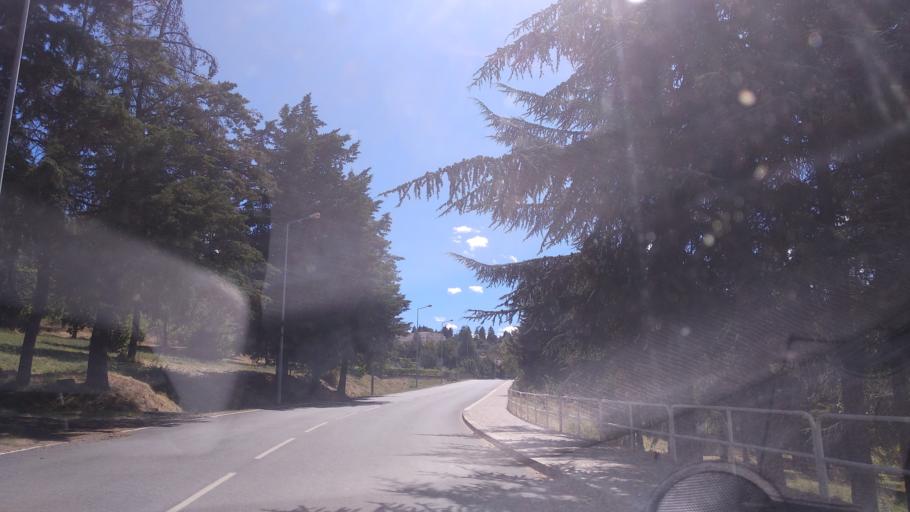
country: PT
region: Braganca
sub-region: Braganca Municipality
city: Braganca
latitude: 41.7970
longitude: -6.7603
